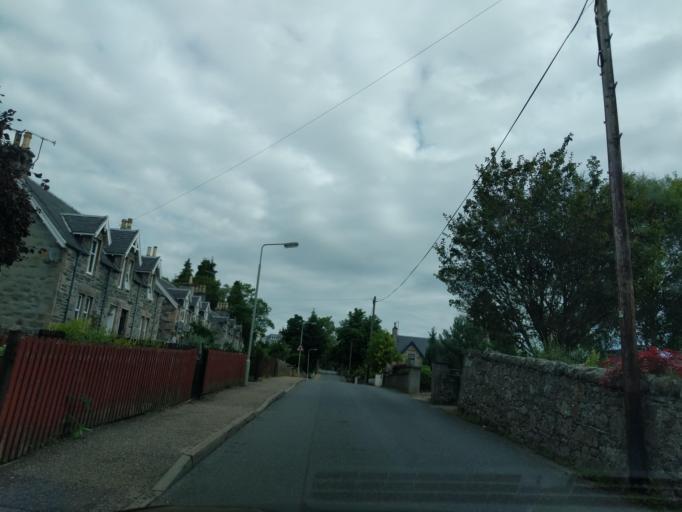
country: GB
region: Scotland
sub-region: Highland
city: Grantown on Spey
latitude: 57.3289
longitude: -3.6136
